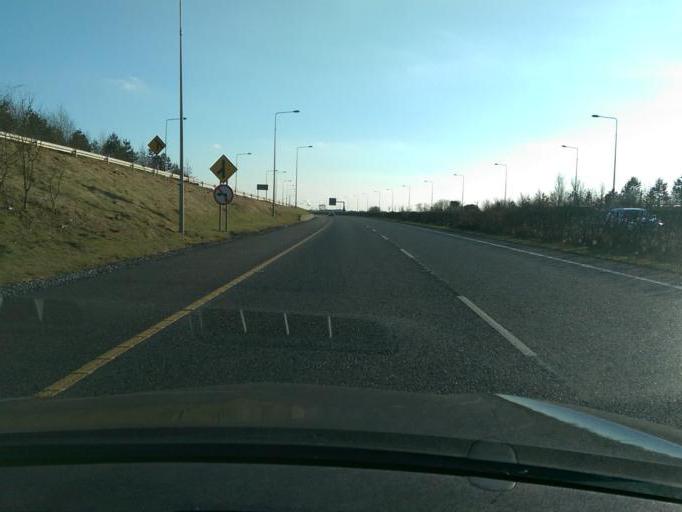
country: IE
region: Leinster
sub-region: Laois
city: Portlaoise
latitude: 53.0489
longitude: -7.2403
